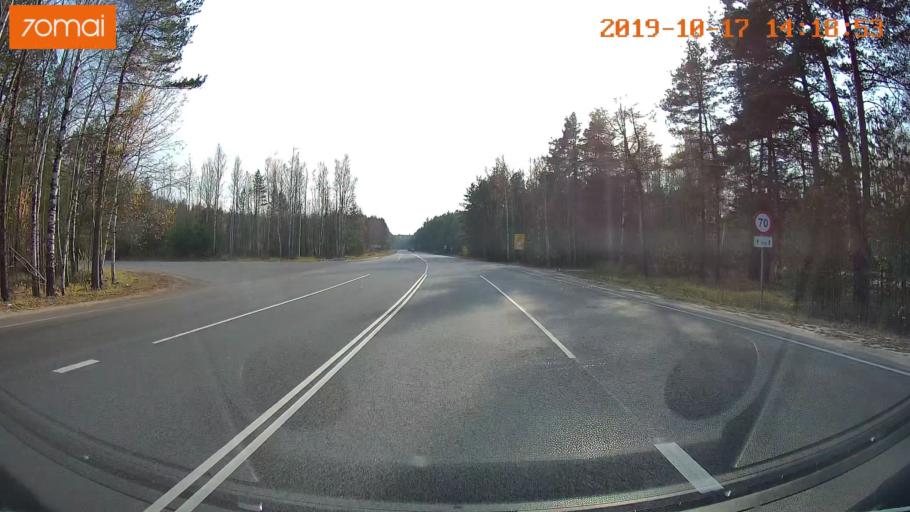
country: RU
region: Rjazan
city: Spas-Klepiki
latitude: 55.0574
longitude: 40.0254
